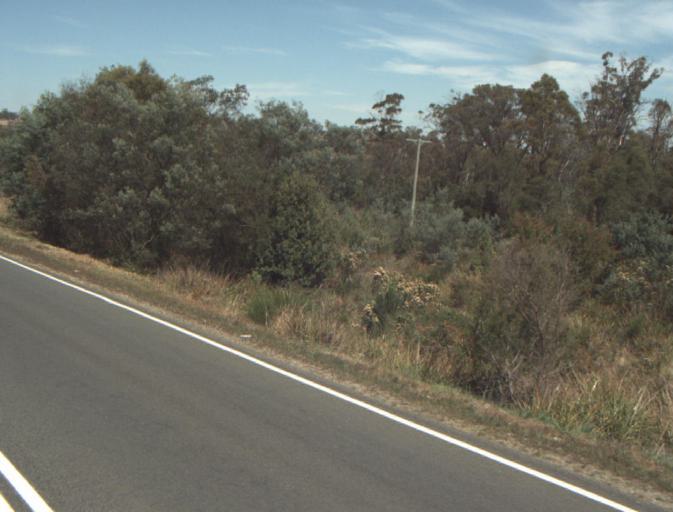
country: AU
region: Tasmania
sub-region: Launceston
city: Mayfield
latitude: -41.3630
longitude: 147.1447
